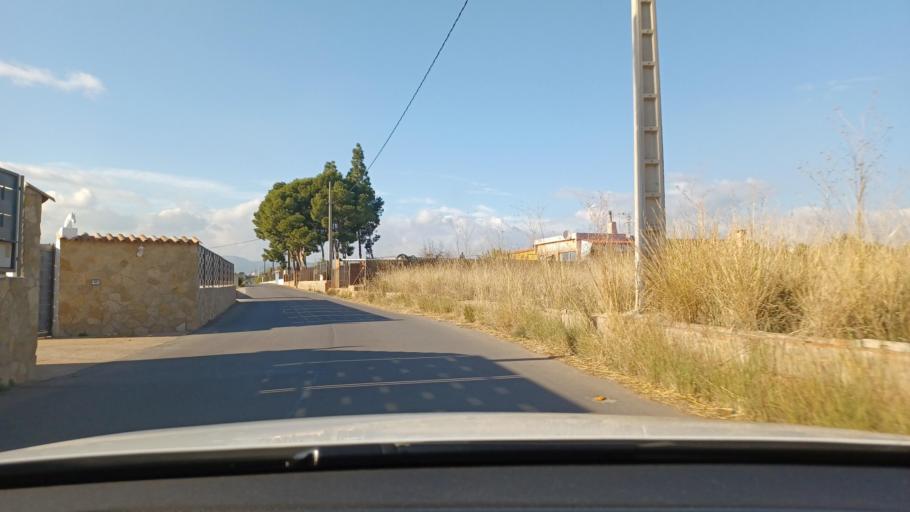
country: ES
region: Valencia
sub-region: Provincia de Castello
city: Onda
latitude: 39.9507
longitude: -0.2274
